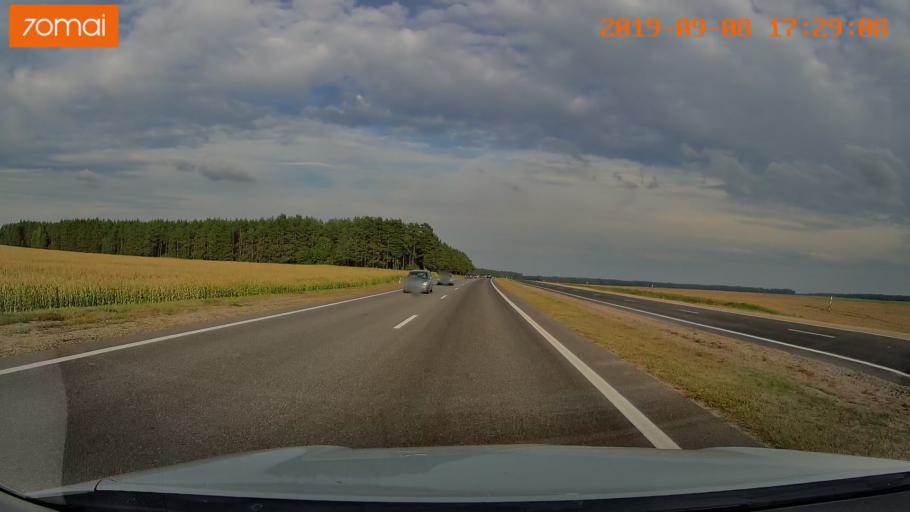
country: BY
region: Grodnenskaya
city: Skidal'
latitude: 53.5840
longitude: 24.4243
